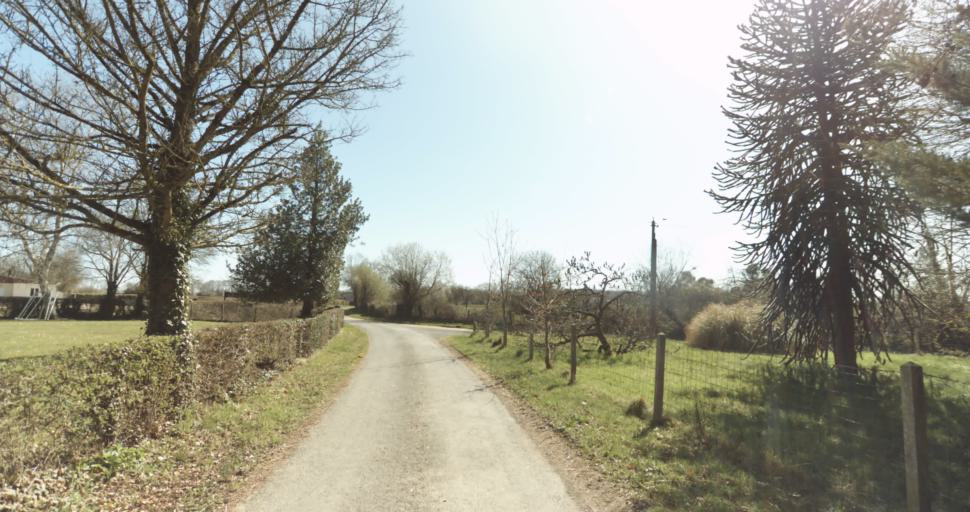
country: FR
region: Lower Normandy
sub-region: Departement du Calvados
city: Livarot
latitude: 49.0223
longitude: 0.0992
